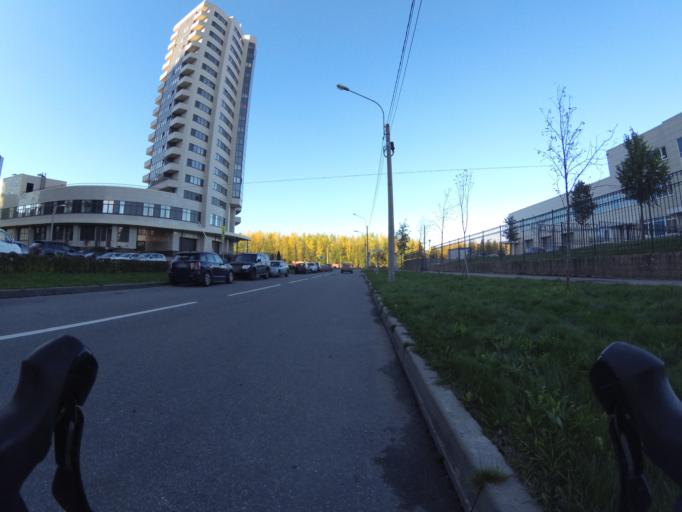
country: RU
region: Leningrad
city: Untolovo
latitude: 60.0003
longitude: 30.1958
